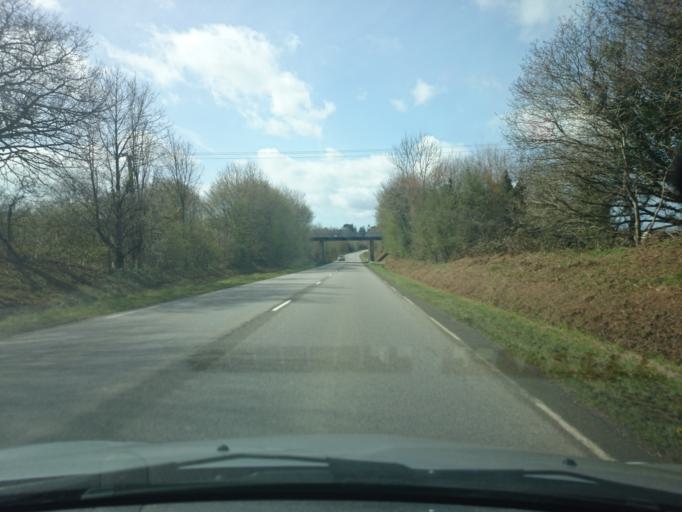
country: FR
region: Brittany
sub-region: Departement du Finistere
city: Gouesnou
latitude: 48.4506
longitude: -4.4503
